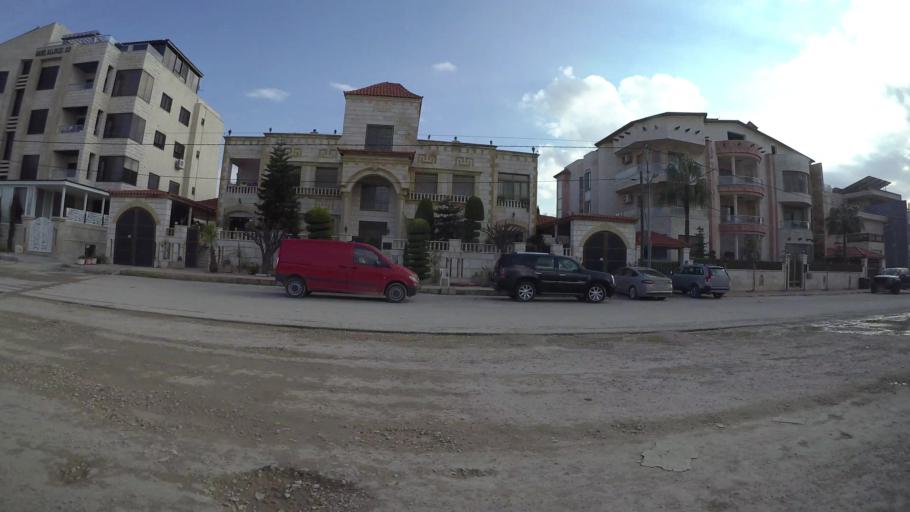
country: JO
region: Amman
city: Al Bunayyat ash Shamaliyah
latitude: 31.9102
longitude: 35.8748
